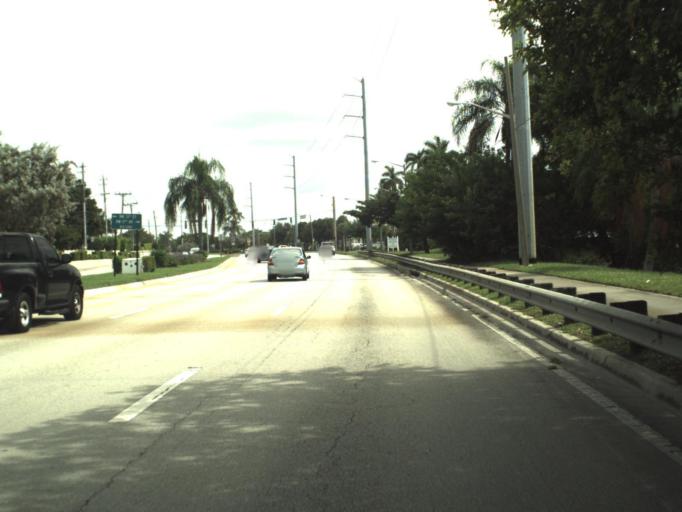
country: US
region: Florida
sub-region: Palm Beach County
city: Delray Beach
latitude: 26.4773
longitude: -80.0902
